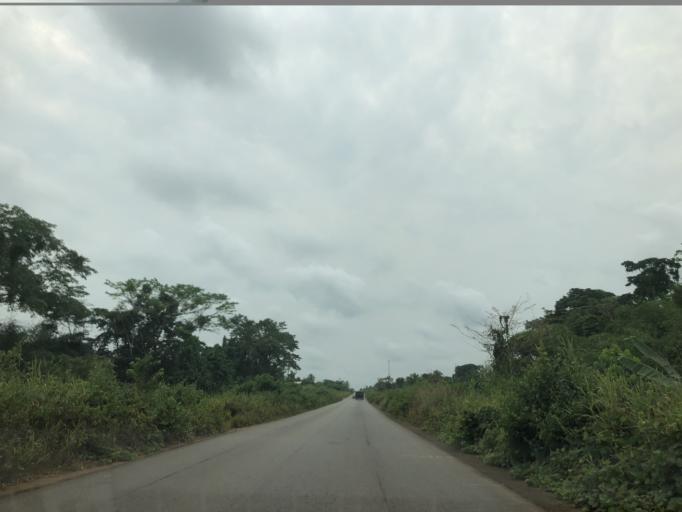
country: CM
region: Littoral
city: Edea
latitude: 3.6481
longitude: 10.1152
